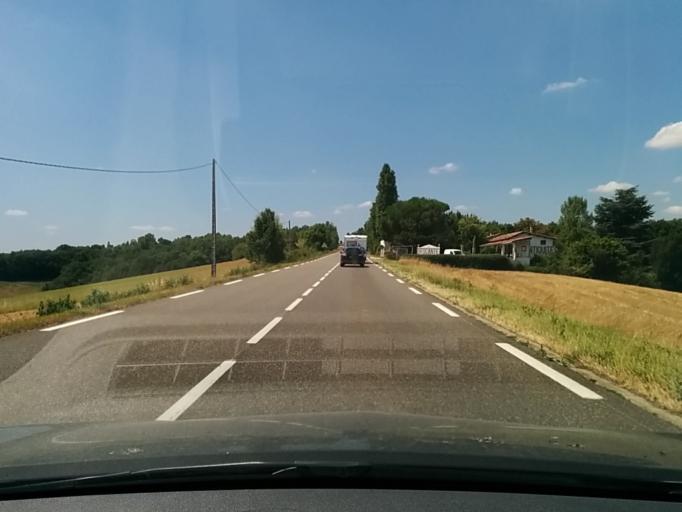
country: FR
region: Midi-Pyrenees
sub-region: Departement du Gers
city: Vic-Fezensac
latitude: 43.7588
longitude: 0.2103
